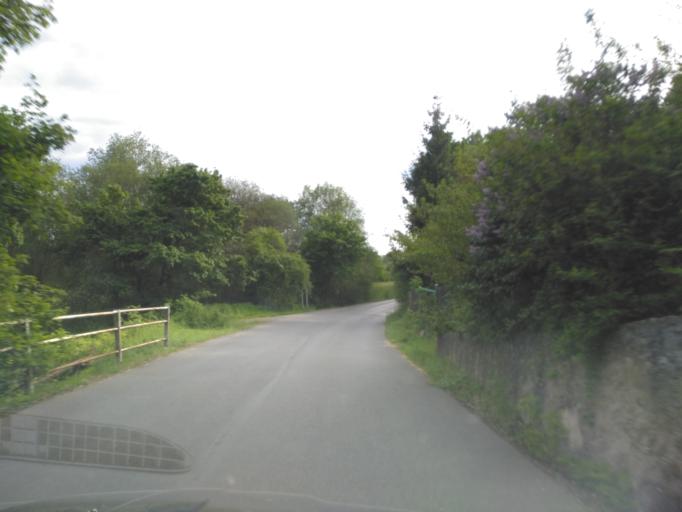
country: CZ
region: Central Bohemia
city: Zdice
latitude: 49.8925
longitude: 13.9587
